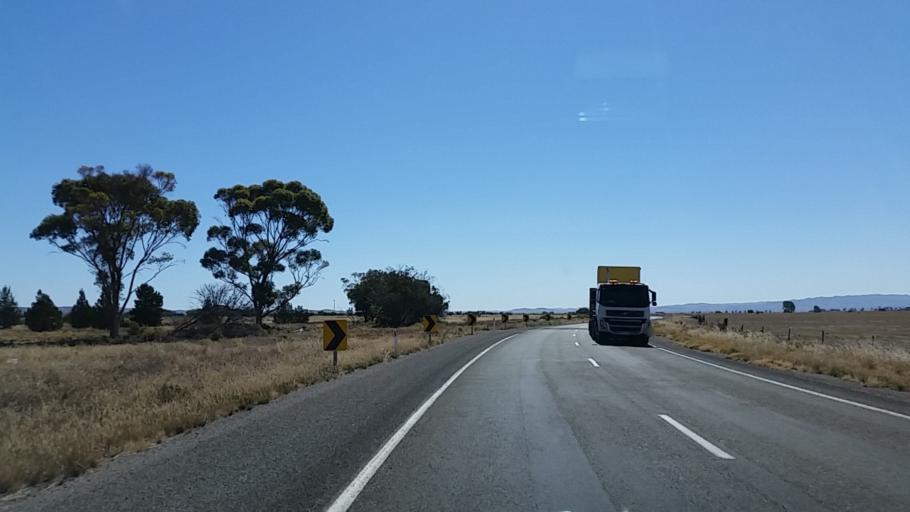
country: AU
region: South Australia
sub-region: Peterborough
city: Peterborough
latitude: -32.7481
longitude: 138.6370
